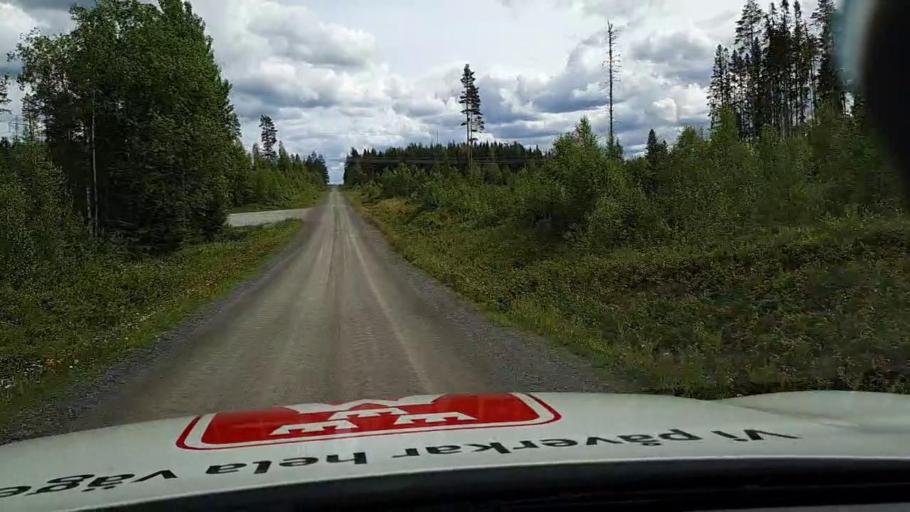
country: SE
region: Jaemtland
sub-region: OEstersunds Kommun
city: Lit
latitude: 63.2930
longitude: 15.3423
